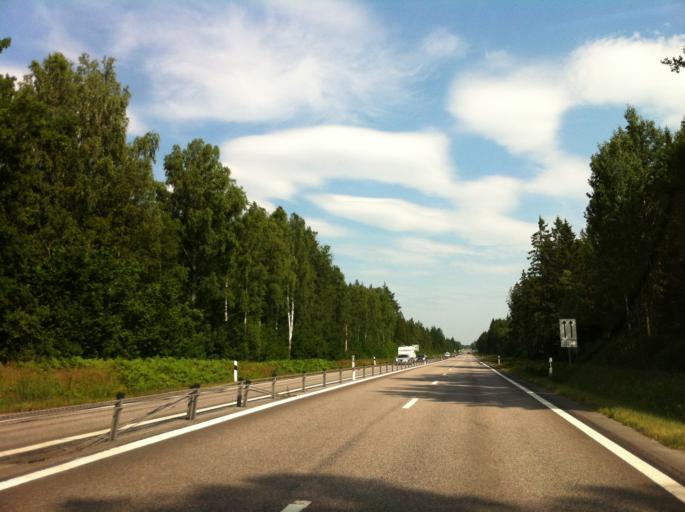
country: SE
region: Kalmar
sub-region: Kalmar Kommun
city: Trekanten
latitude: 56.7178
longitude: 16.0406
